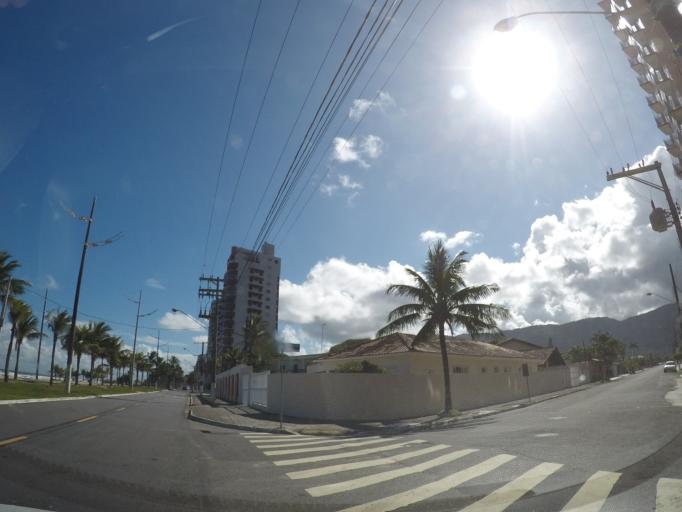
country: BR
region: Sao Paulo
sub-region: Mongagua
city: Mongagua
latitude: -24.0696
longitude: -46.5657
